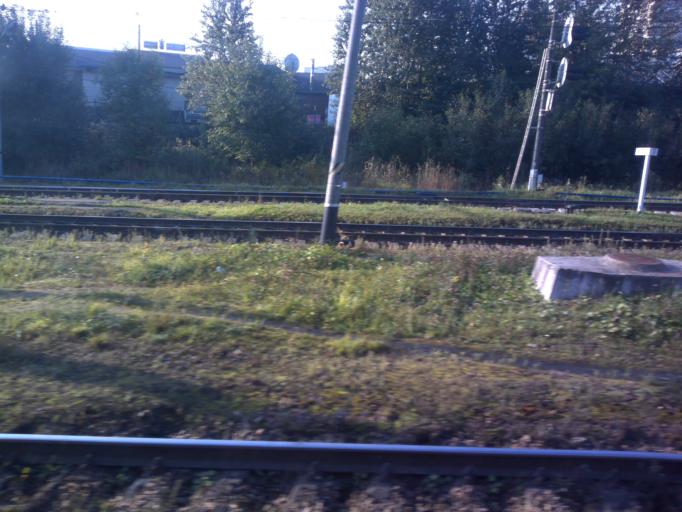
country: RU
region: Leningrad
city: Kalininskiy
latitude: 59.9879
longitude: 30.4271
